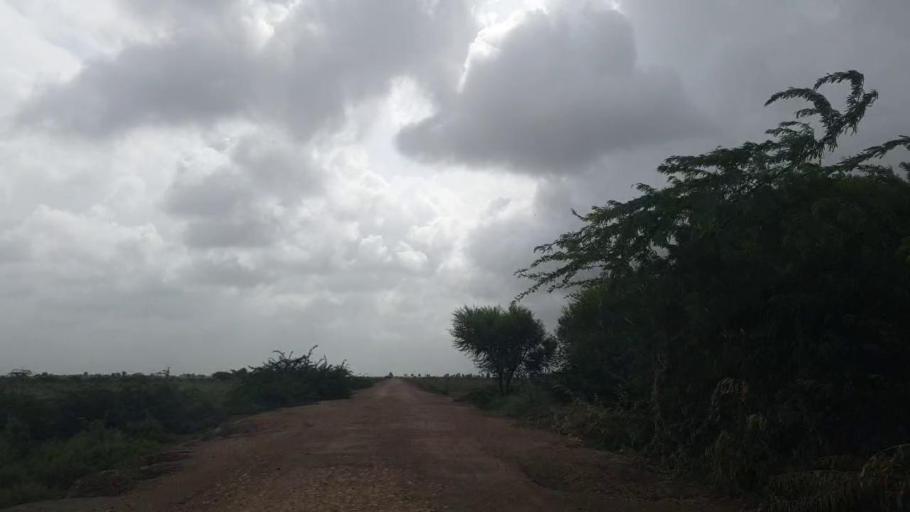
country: PK
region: Sindh
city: Tando Bago
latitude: 24.8426
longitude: 69.1341
